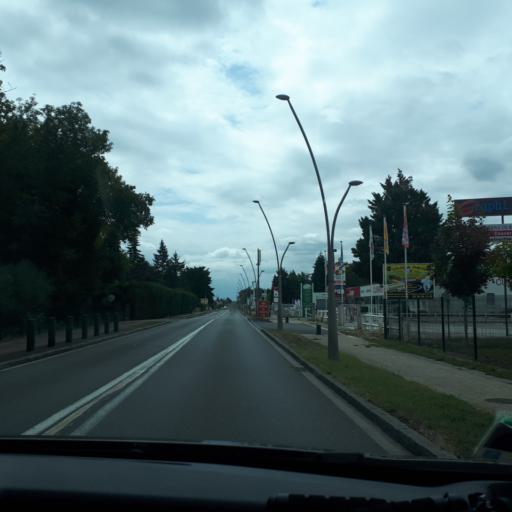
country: FR
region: Centre
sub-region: Departement du Loiret
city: Saint-Pere-sur-Loire
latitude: 47.7928
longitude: 2.3803
